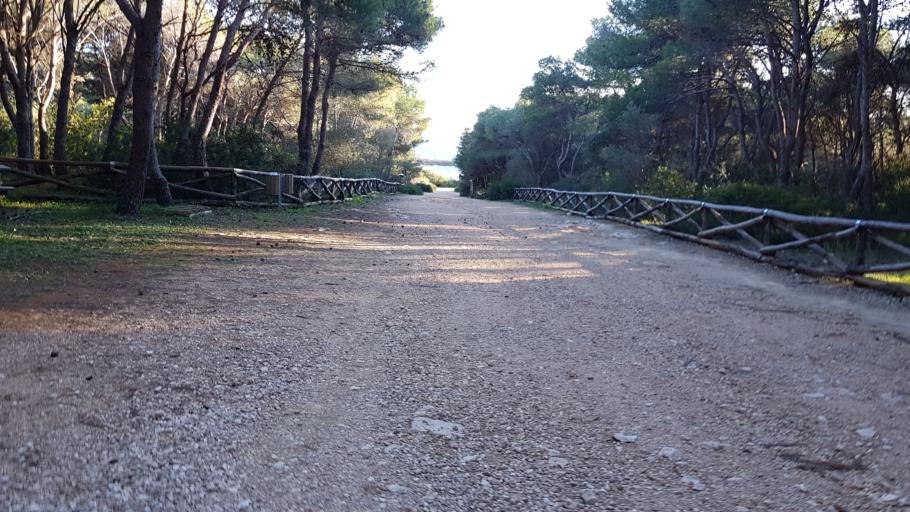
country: IT
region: Apulia
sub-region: Provincia di Lecce
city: Nardo
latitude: 40.1490
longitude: 17.9722
